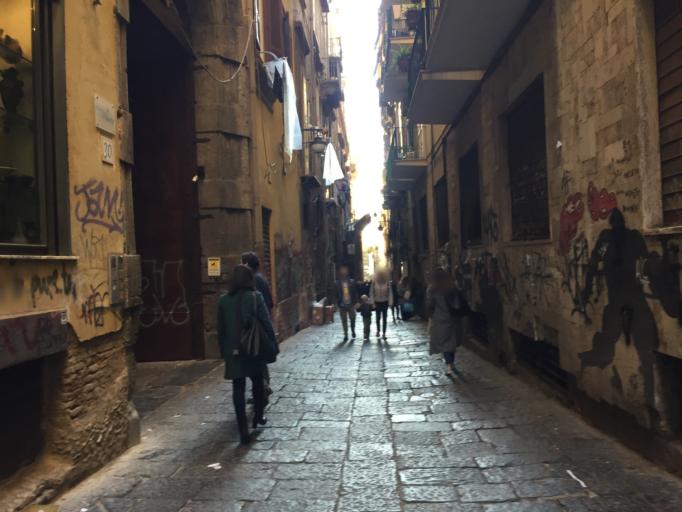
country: IT
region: Campania
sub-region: Provincia di Napoli
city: Napoli
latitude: 40.8494
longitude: 14.2557
